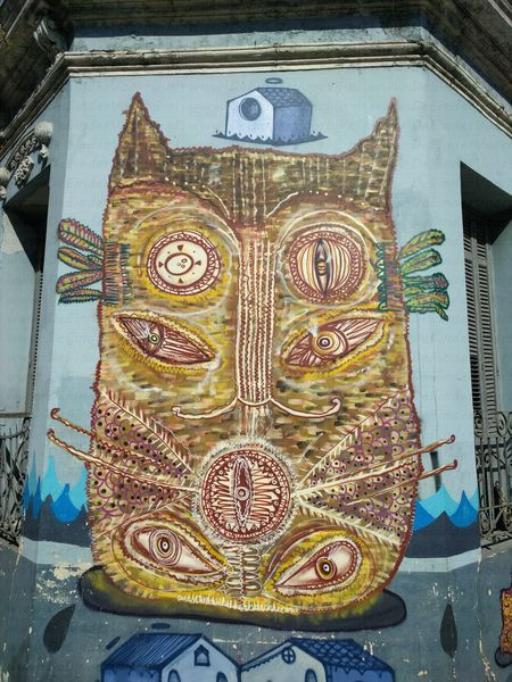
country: UY
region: Montevideo
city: Montevideo
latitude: -34.9099
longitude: -56.2093
